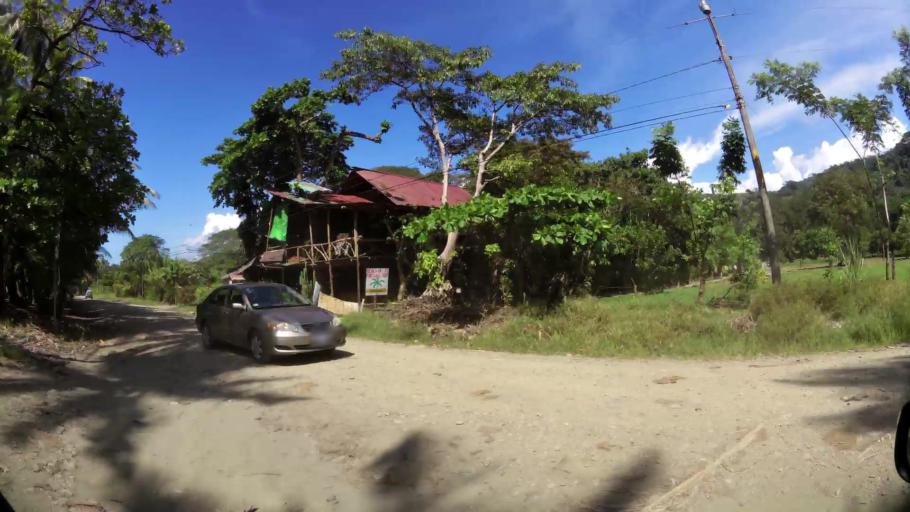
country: CR
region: San Jose
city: San Isidro
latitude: 9.2506
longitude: -83.8625
